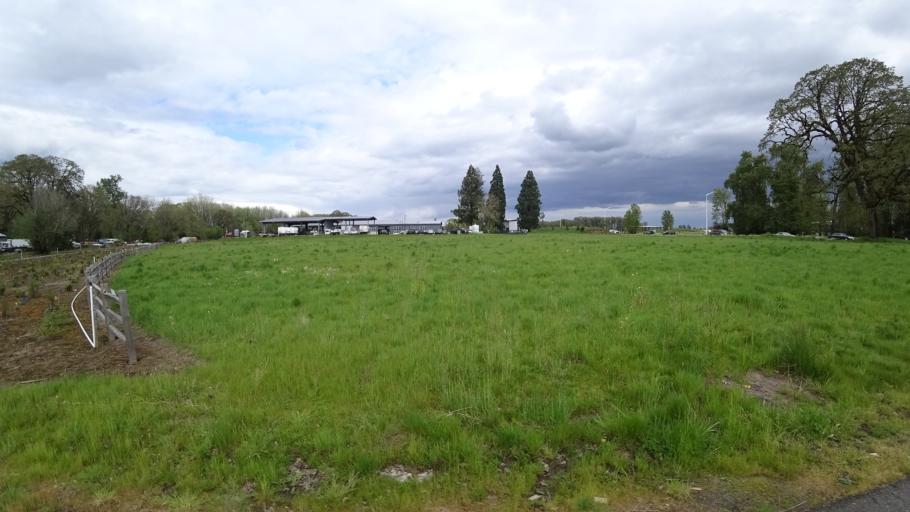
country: US
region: Oregon
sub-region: Washington County
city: Hillsboro
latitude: 45.5518
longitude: -122.9528
